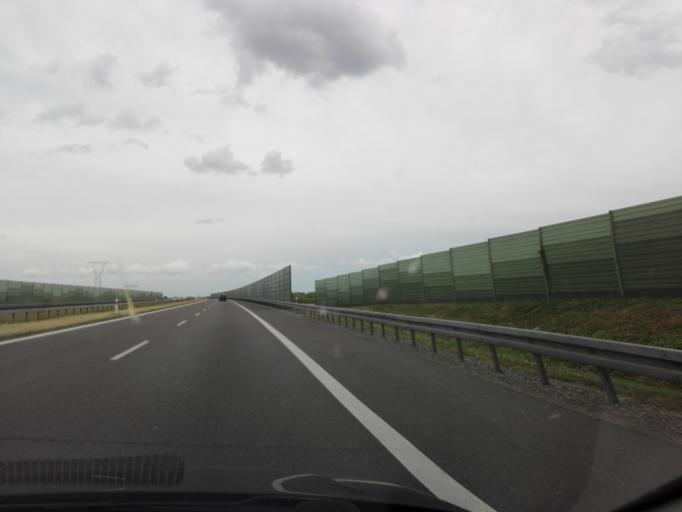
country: PL
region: Lublin Voivodeship
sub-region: Powiat lubelski
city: Garbow
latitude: 51.3782
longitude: 22.3008
